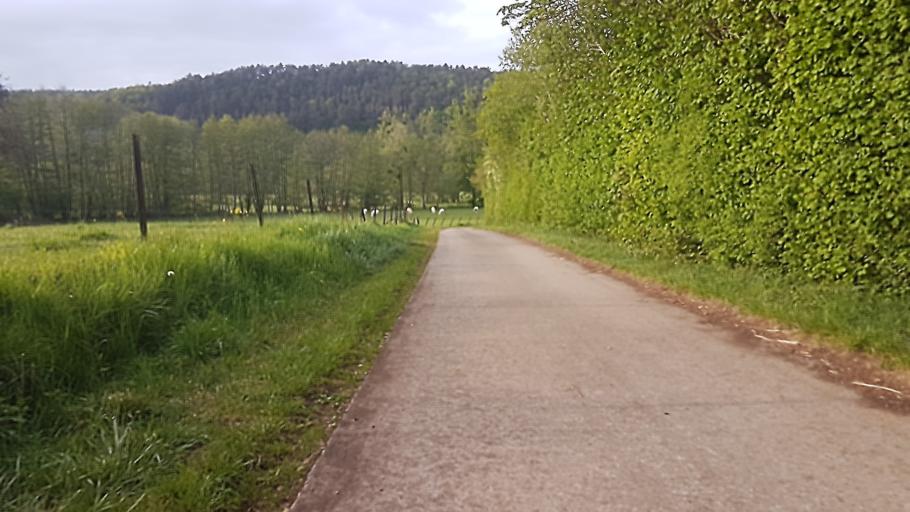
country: FR
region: Champagne-Ardenne
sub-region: Departement des Ardennes
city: Vireux-Molhain
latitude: 50.0725
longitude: 4.6147
